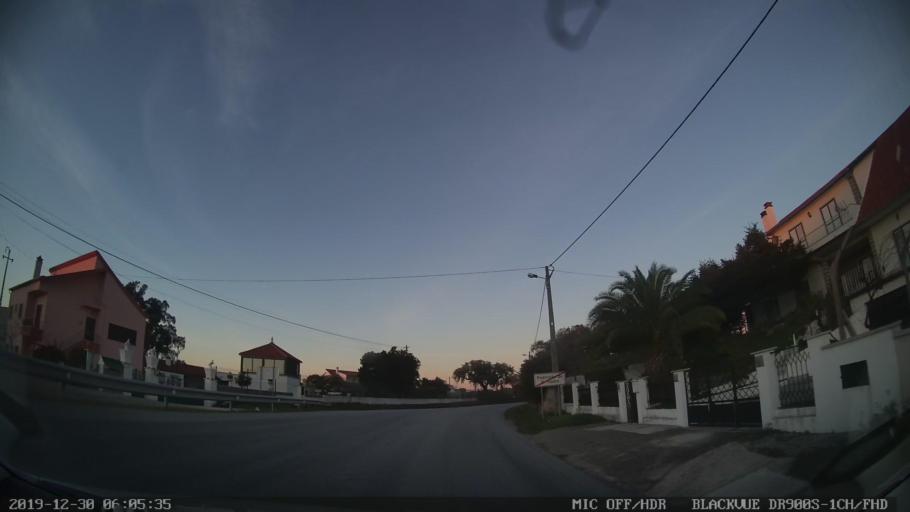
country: PT
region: Castelo Branco
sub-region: Penamacor
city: Penamacor
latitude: 40.0916
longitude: -7.2365
